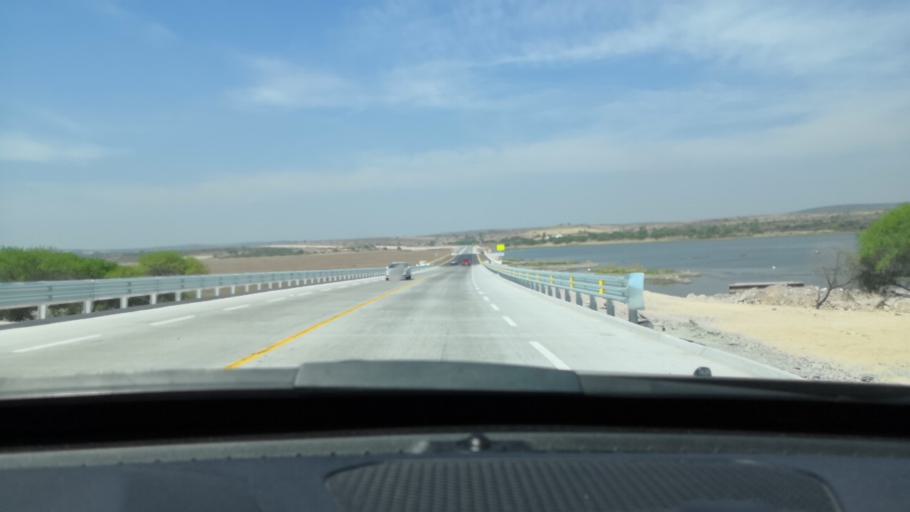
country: MX
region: Guanajuato
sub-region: Purisima del Rincon
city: Potrerillos (Guanajal)
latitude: 21.0836
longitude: -101.8395
